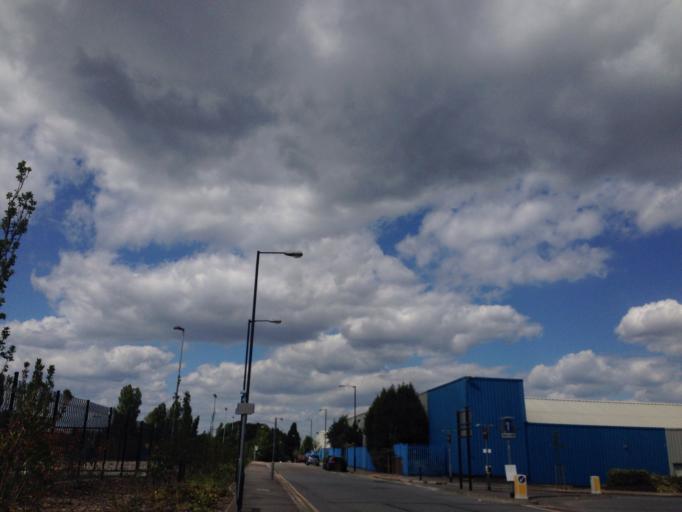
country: GB
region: England
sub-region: Greater London
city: Acton
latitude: 51.5318
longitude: -0.2782
